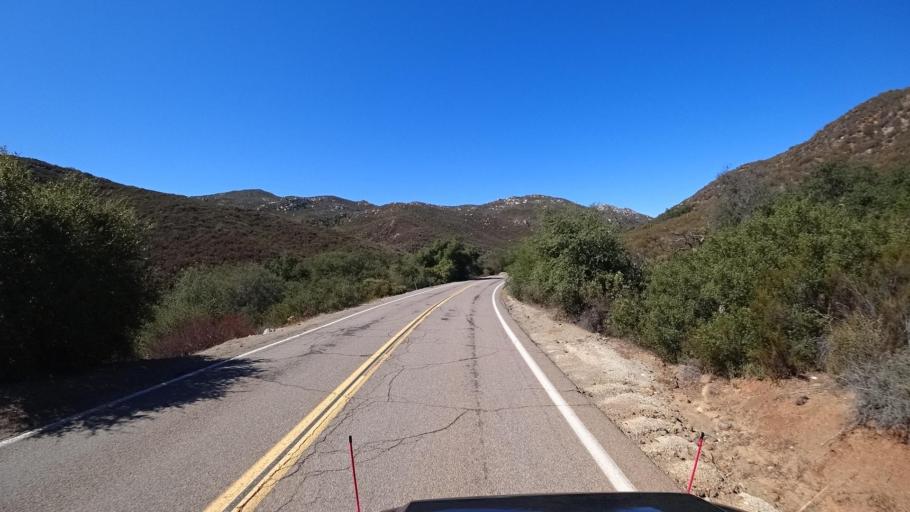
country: US
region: California
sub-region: San Diego County
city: Alpine
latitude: 32.7049
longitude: -116.7180
